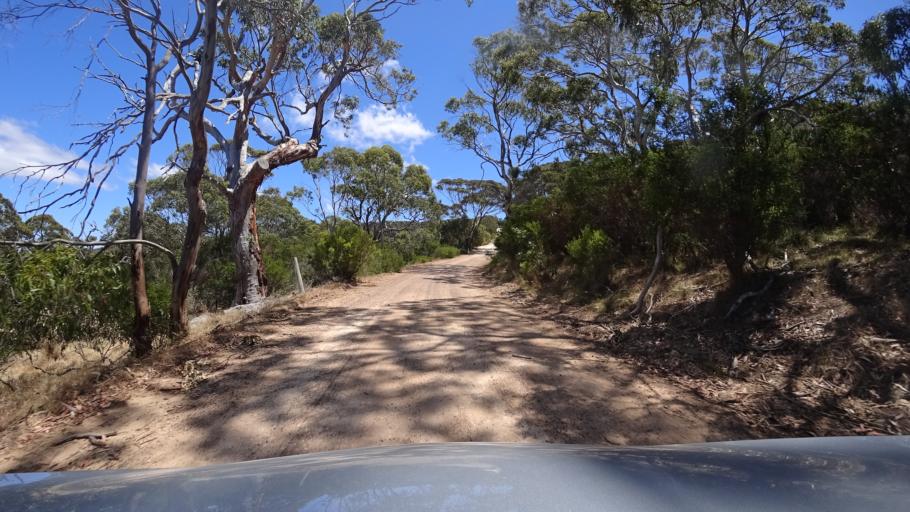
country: AU
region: South Australia
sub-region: Yankalilla
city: Normanville
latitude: -35.7851
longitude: 138.0646
